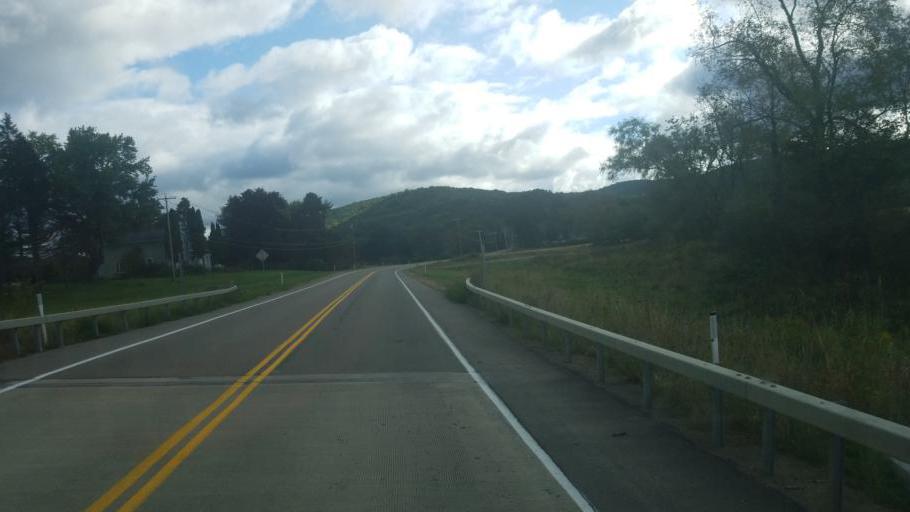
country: US
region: New York
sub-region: Cattaraugus County
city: Weston Mills
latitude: 42.0887
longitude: -78.3643
